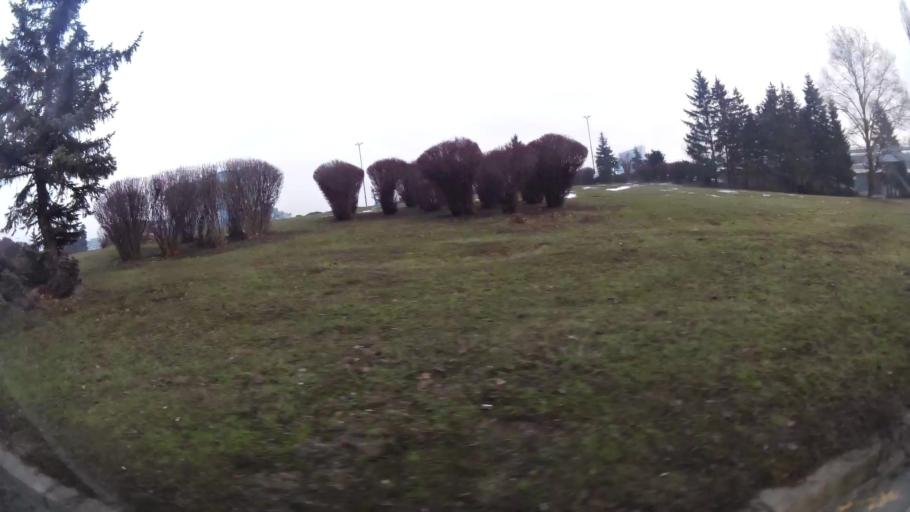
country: BG
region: Sofia-Capital
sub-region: Stolichna Obshtina
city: Sofia
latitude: 42.6535
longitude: 23.2808
